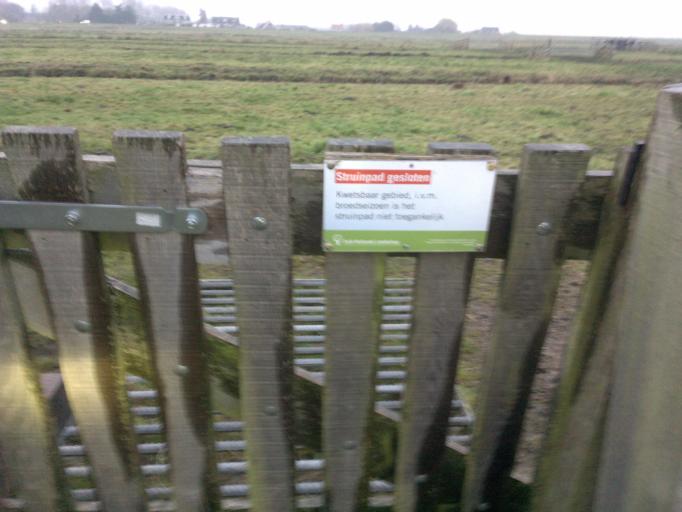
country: NL
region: North Holland
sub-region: Gemeente Bloemendaal
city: Bennebroek
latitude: 52.3038
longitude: 4.5973
